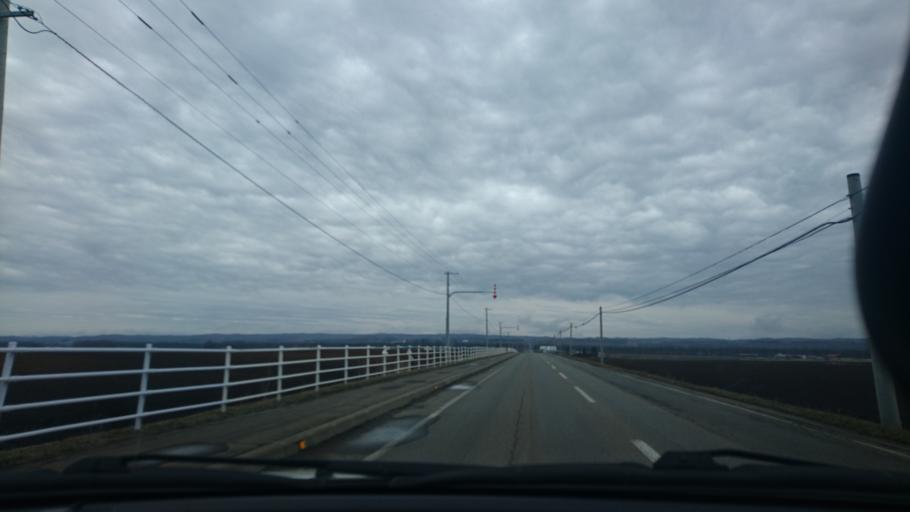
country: JP
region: Hokkaido
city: Otofuke
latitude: 42.9938
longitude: 143.2238
